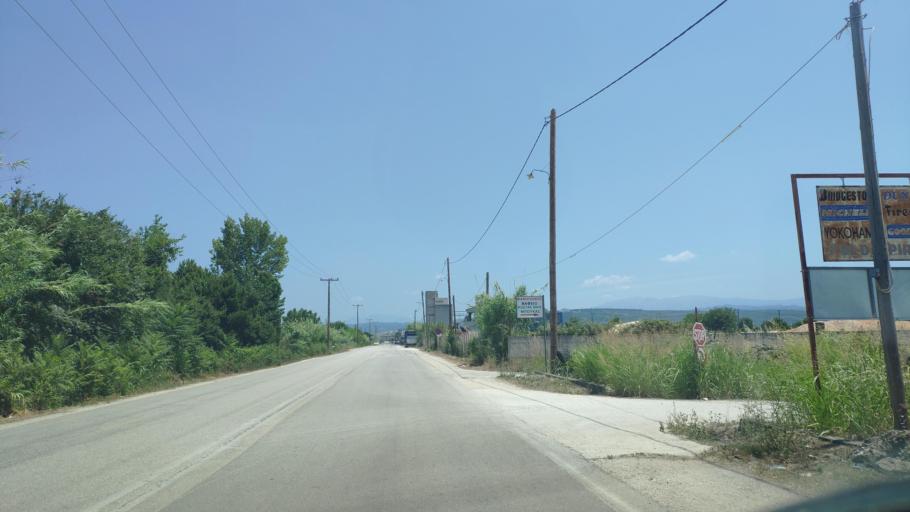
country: GR
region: Epirus
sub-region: Nomos Artas
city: Kostakioi
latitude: 39.1257
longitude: 20.9428
